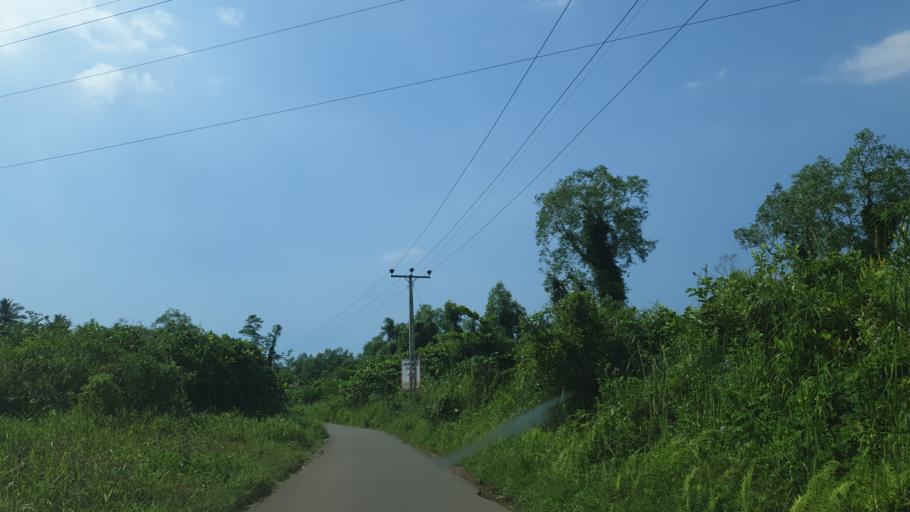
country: LK
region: Western
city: Panadura
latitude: 6.7407
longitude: 79.9510
